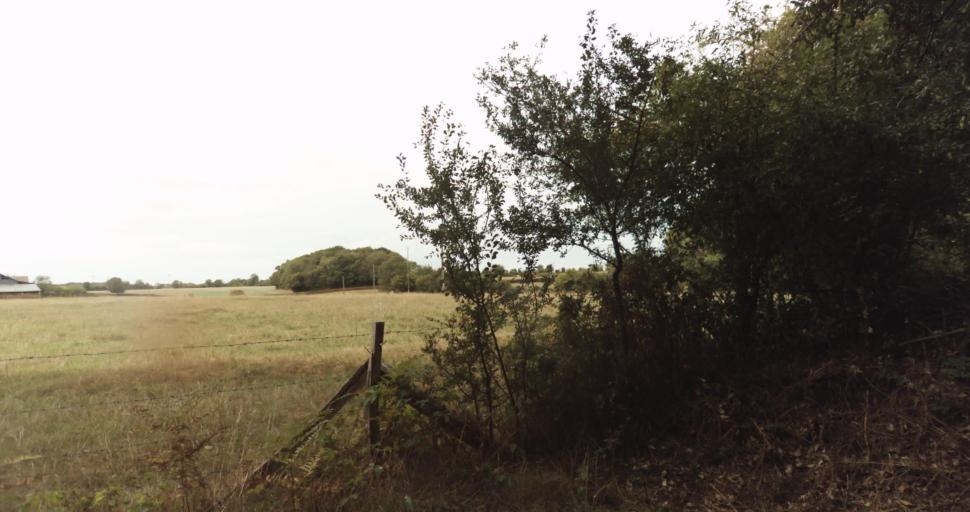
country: FR
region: Lower Normandy
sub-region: Departement du Calvados
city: Orbec
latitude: 48.9556
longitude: 0.3797
